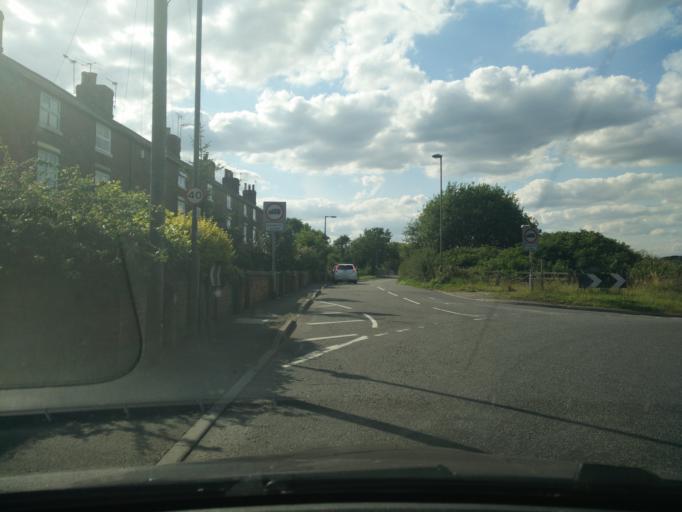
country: GB
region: England
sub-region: Derbyshire
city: Ilkeston
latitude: 52.9471
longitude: -1.3094
